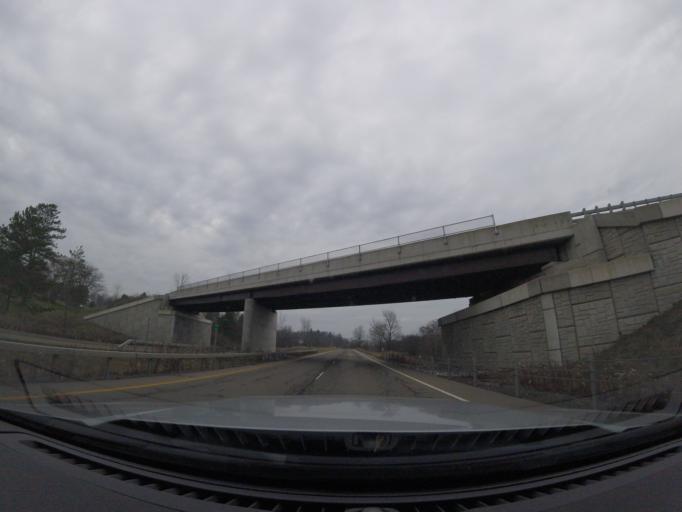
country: US
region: New York
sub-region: Schuyler County
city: Watkins Glen
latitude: 42.4213
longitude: -76.9037
